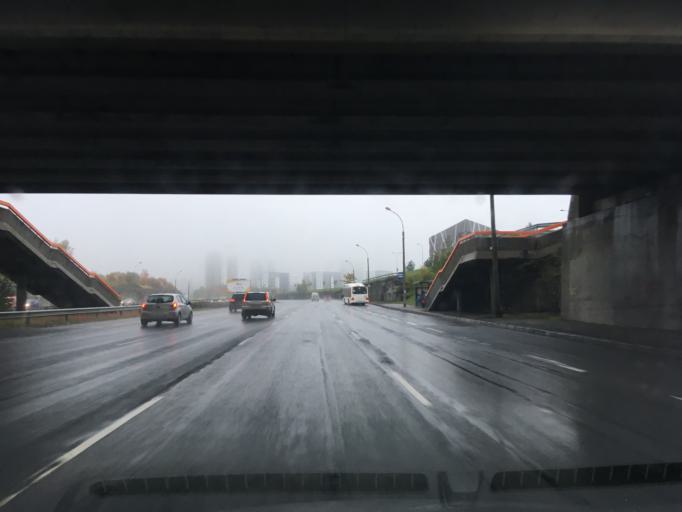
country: EE
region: Harju
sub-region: Tallinna linn
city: Tallinn
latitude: 59.4349
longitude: 24.7981
